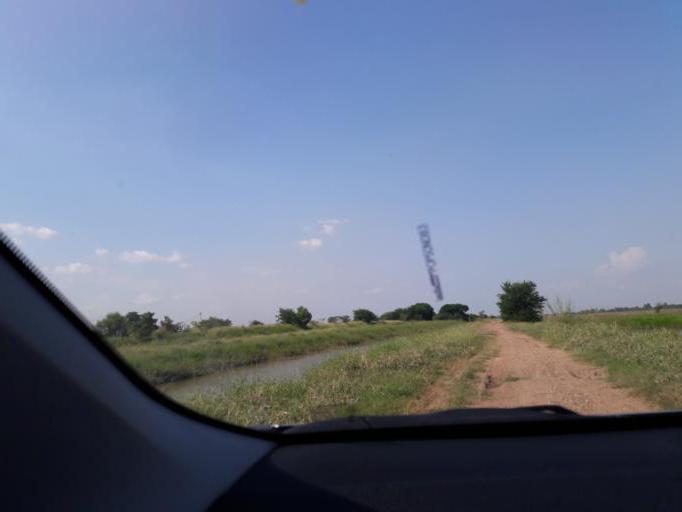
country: TH
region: Ang Thong
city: Ang Thong
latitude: 14.5521
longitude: 100.4066
